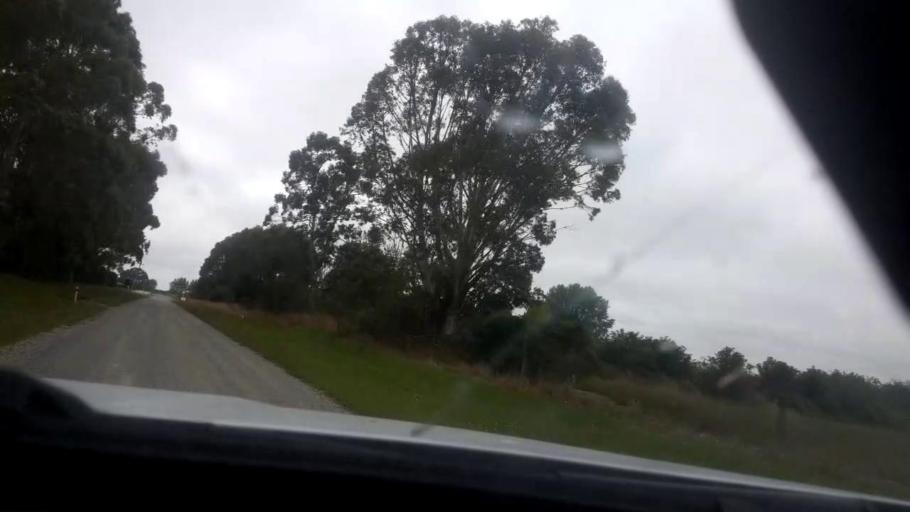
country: NZ
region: Canterbury
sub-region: Timaru District
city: Pleasant Point
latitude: -44.2883
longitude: 171.2125
